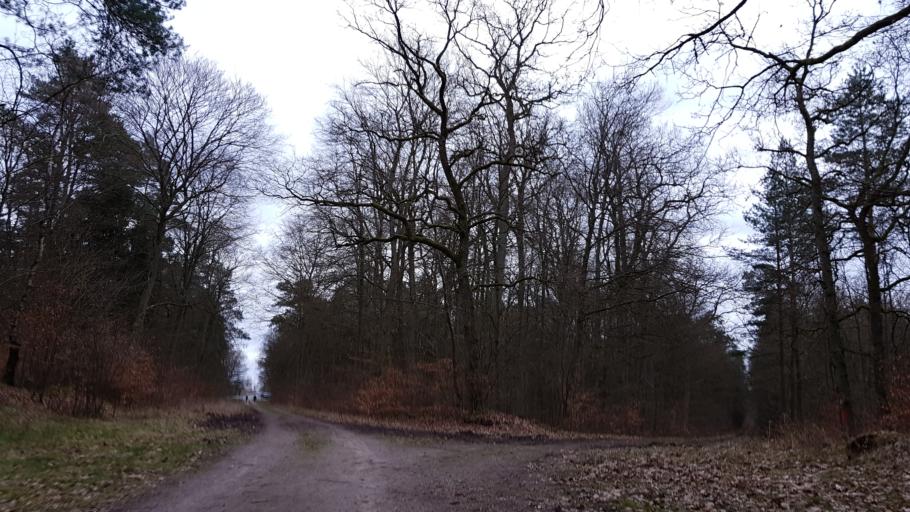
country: DE
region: Lower Saxony
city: Deutsch Evern
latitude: 53.2160
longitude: 10.4379
